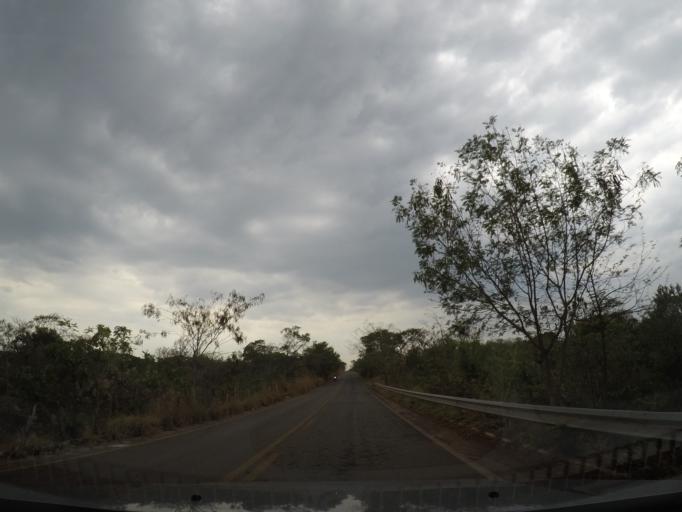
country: BR
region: Goias
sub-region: Pirenopolis
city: Pirenopolis
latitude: -15.8530
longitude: -48.9379
